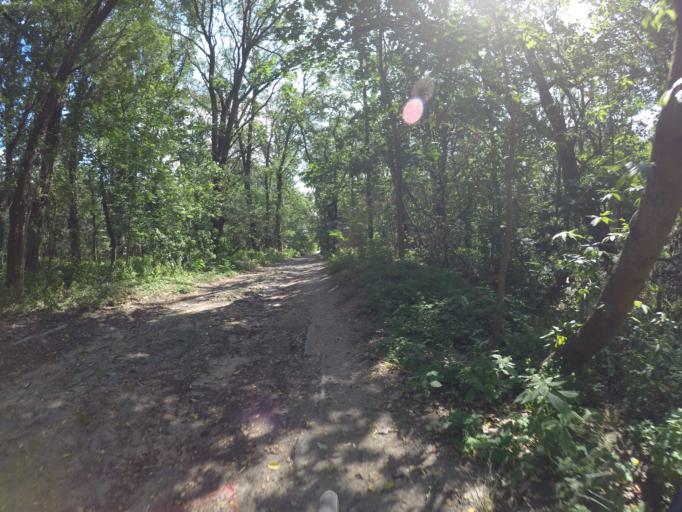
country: DE
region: Brandenburg
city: Werder
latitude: 52.4092
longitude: 12.9819
